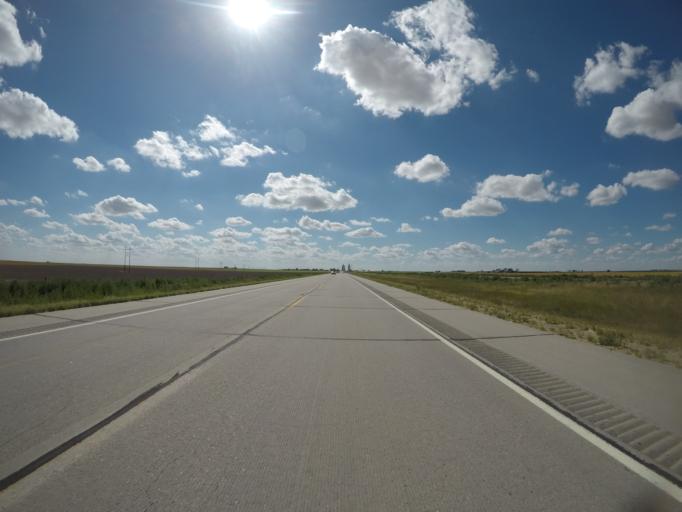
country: US
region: Colorado
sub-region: Phillips County
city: Holyoke
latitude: 40.6084
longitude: -102.4471
